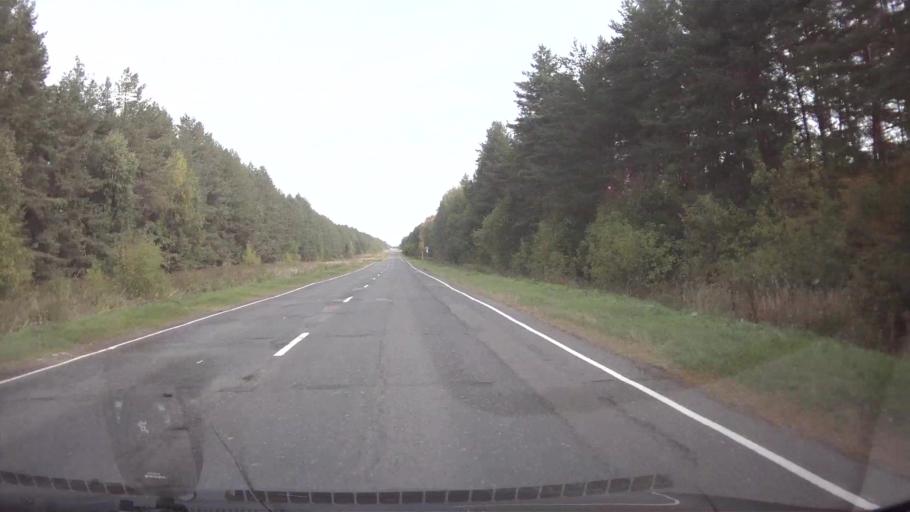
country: RU
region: Mariy-El
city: Kuzhener
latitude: 56.8223
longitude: 48.7194
